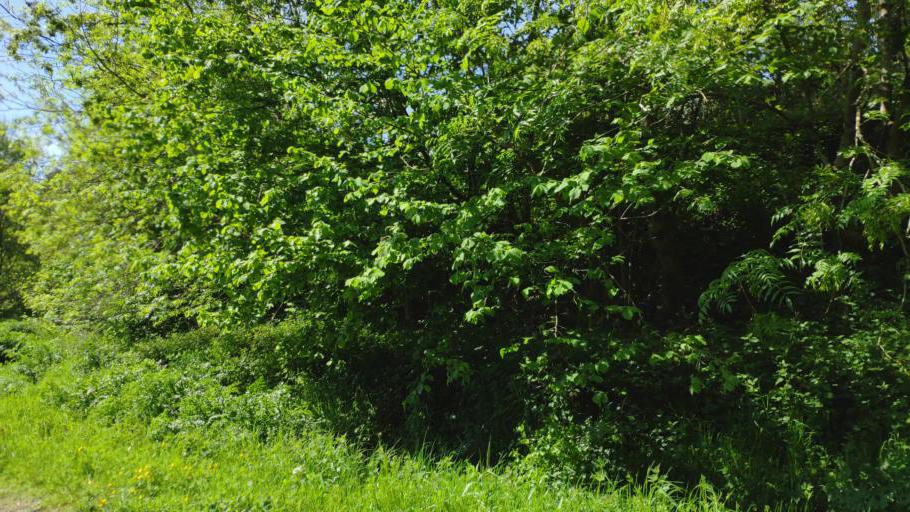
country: IE
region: Munster
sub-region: County Cork
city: Blarney
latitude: 51.9405
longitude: -8.5640
